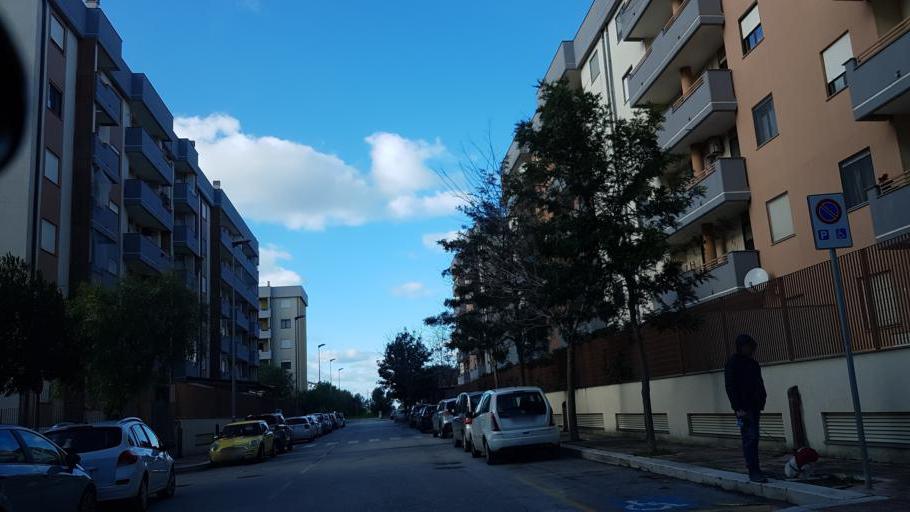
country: IT
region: Apulia
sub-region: Provincia di Brindisi
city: Brindisi
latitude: 40.6504
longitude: 17.9221
